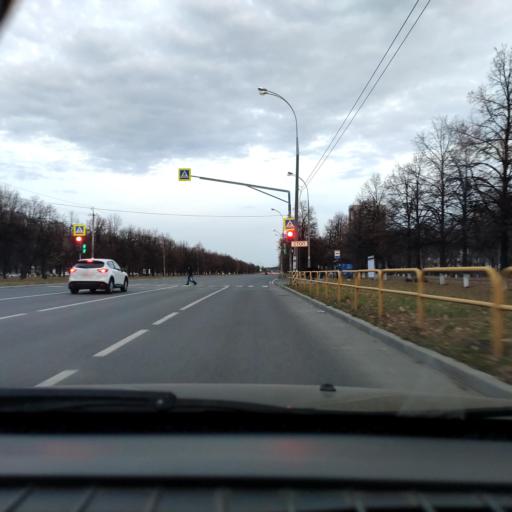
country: RU
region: Samara
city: Tol'yatti
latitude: 53.5191
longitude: 49.2844
